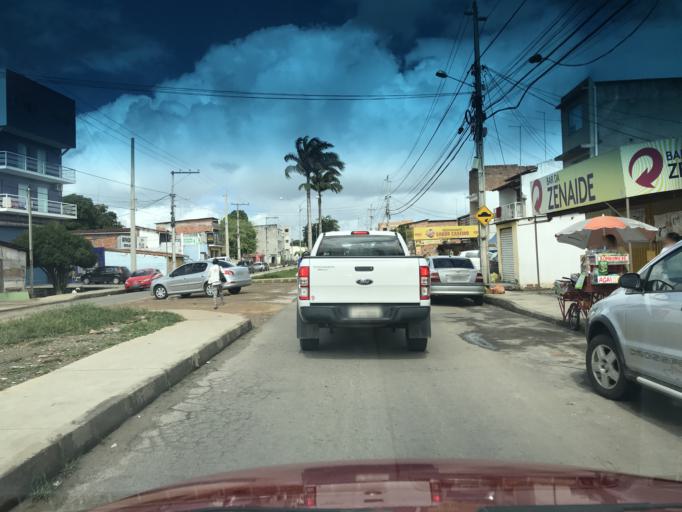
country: BR
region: Bahia
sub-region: Santo Antonio De Jesus
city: Santo Antonio de Jesus
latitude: -12.9711
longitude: -39.2722
